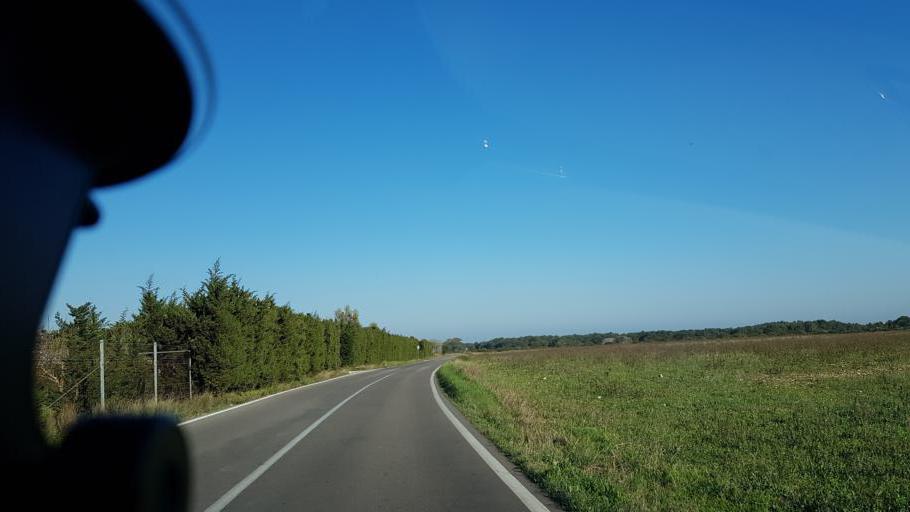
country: IT
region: Apulia
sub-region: Provincia di Lecce
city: Struda
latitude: 40.3924
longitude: 18.2811
